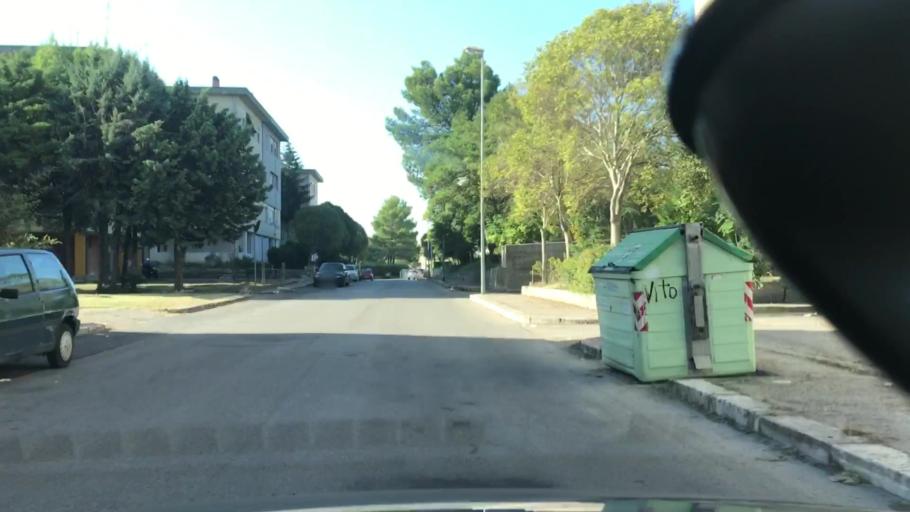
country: IT
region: Basilicate
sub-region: Provincia di Matera
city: Matera
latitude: 40.6874
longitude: 16.5857
